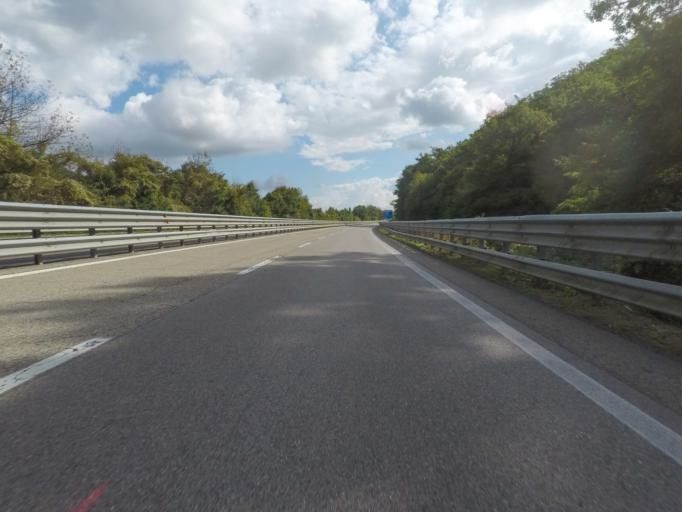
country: IT
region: Tuscany
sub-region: Province of Arezzo
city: Lucignano
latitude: 43.2561
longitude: 11.6995
